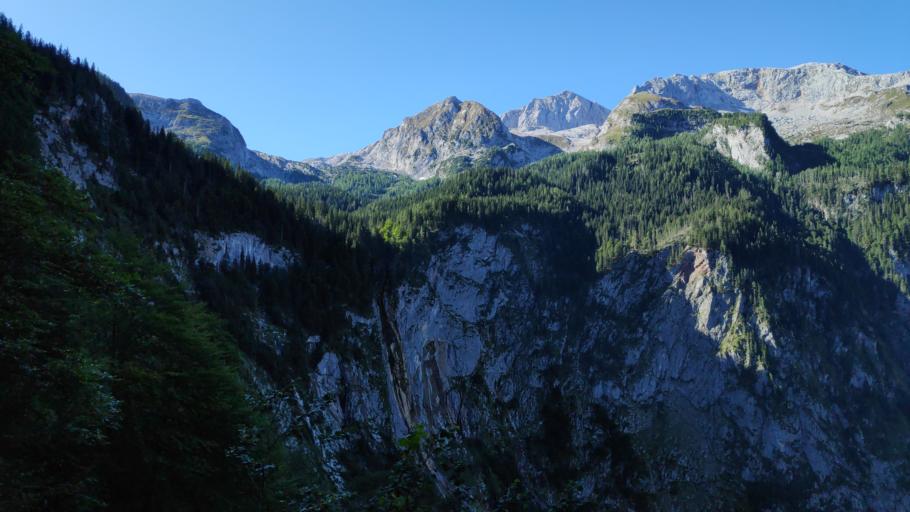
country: DE
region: Bavaria
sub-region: Upper Bavaria
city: Schoenau am Koenigssee
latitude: 47.5088
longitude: 13.0171
